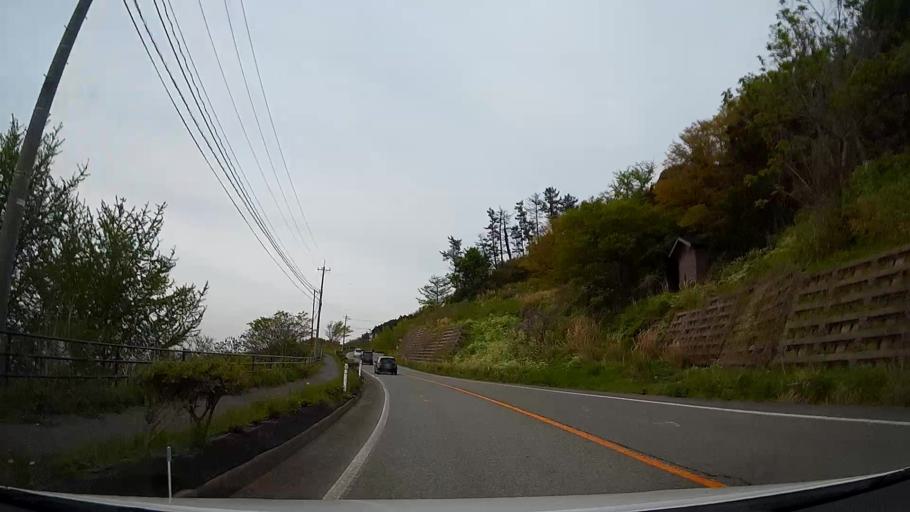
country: JP
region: Ishikawa
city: Nanao
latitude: 37.4196
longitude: 136.9870
